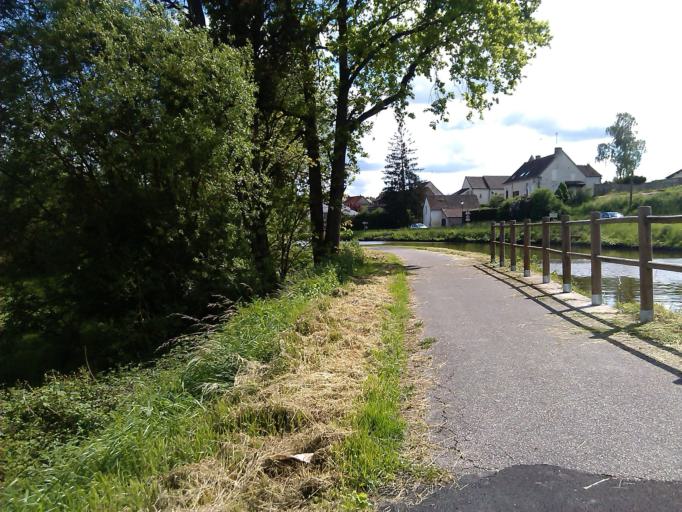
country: FR
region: Bourgogne
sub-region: Departement de Saone-et-Loire
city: Ecuisses
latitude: 46.7754
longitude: 4.5436
